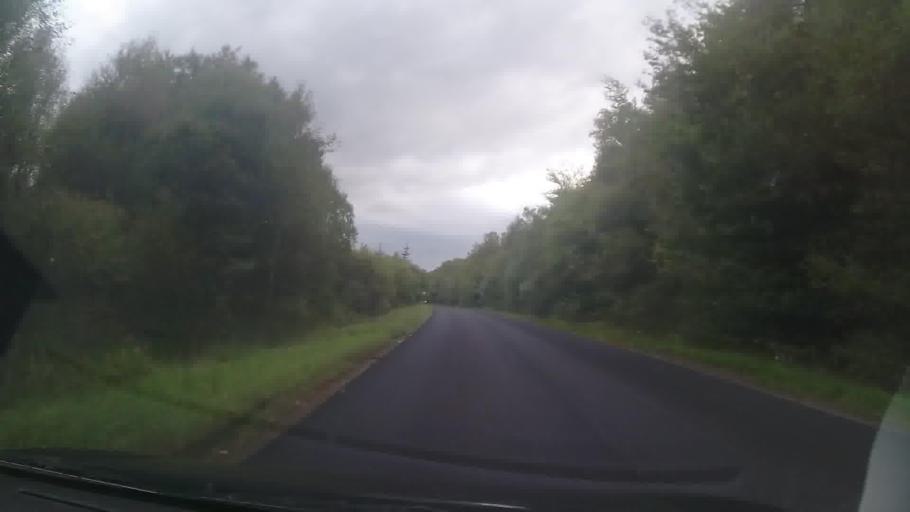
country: GB
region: Scotland
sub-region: Argyll and Bute
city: Garelochhead
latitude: 56.2354
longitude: -4.9683
